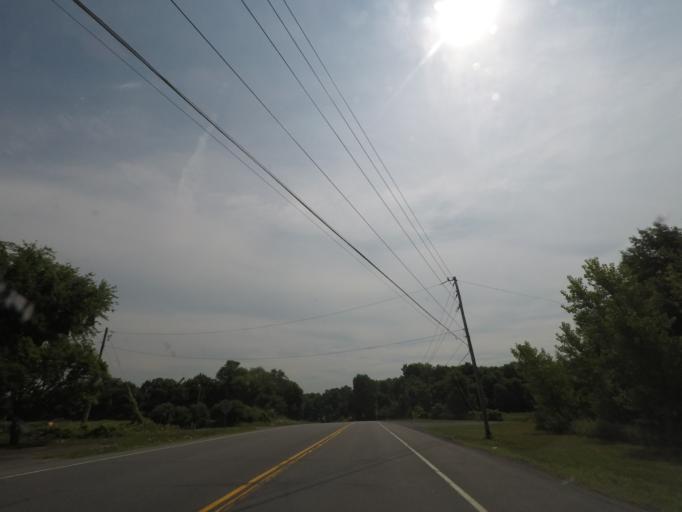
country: US
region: New York
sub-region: Saratoga County
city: Mechanicville
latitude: 42.8851
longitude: -73.6988
